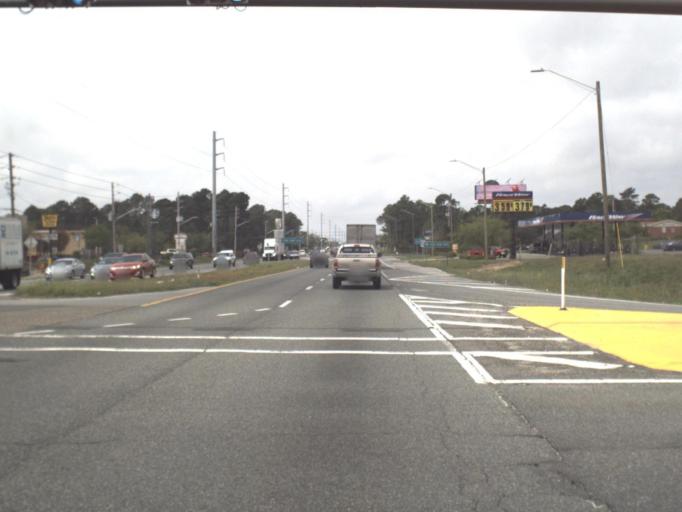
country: US
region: Florida
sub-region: Santa Rosa County
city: Tiger Point
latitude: 30.3899
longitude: -87.0668
